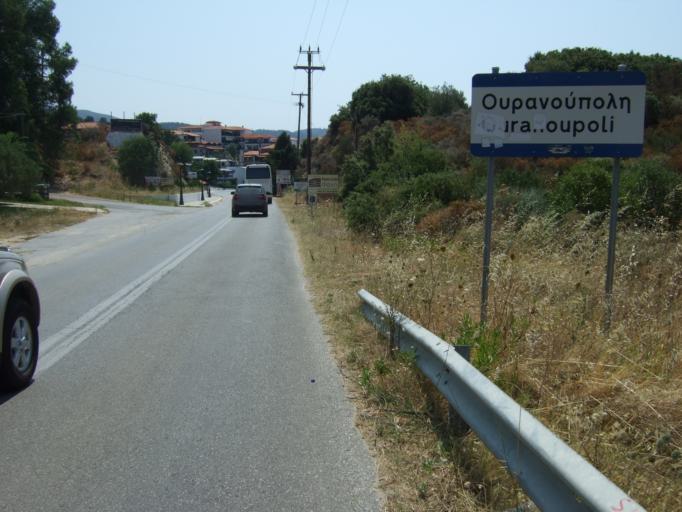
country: GR
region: Central Macedonia
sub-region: Nomos Chalkidikis
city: Ouranoupolis
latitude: 40.3329
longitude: 23.9745
